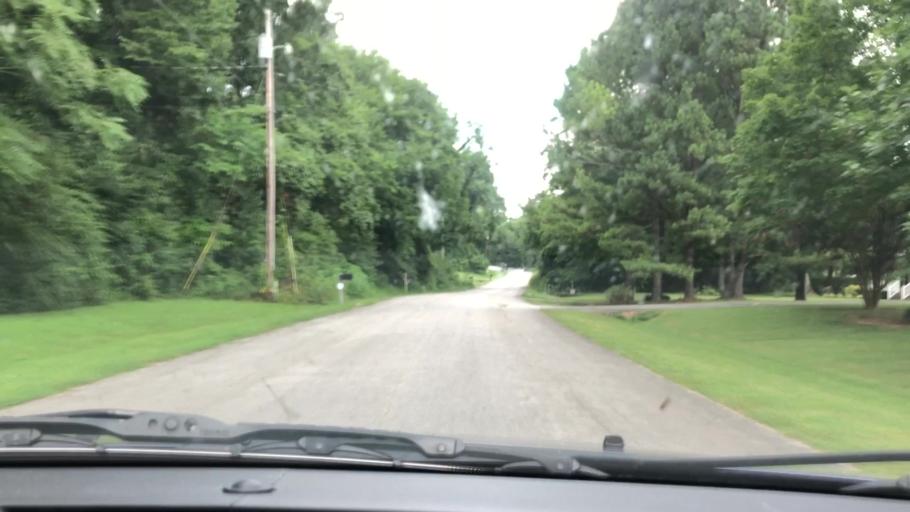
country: US
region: Tennessee
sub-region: Maury County
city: Columbia
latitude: 35.6776
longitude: -86.9915
